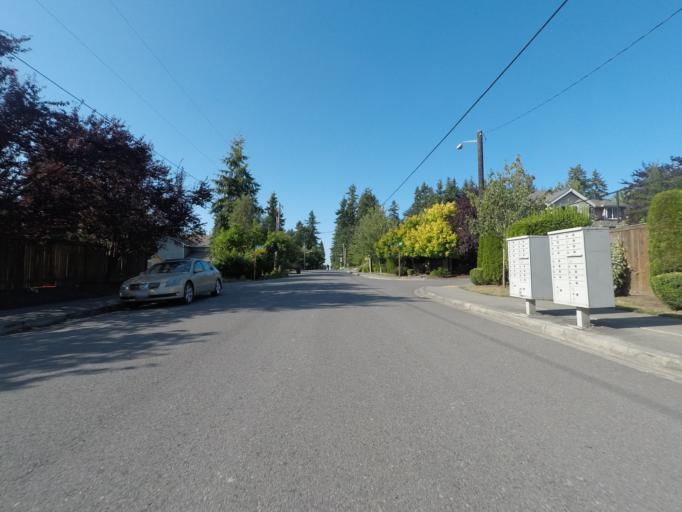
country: US
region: Washington
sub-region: King County
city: Inglewood-Finn Hill
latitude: 47.7360
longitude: -122.2329
